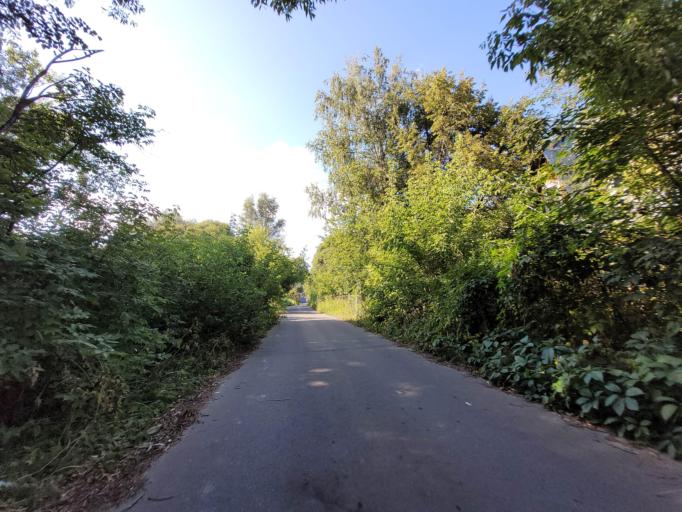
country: RU
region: Moskovskaya
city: Konobeyevo
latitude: 55.4126
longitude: 38.6953
